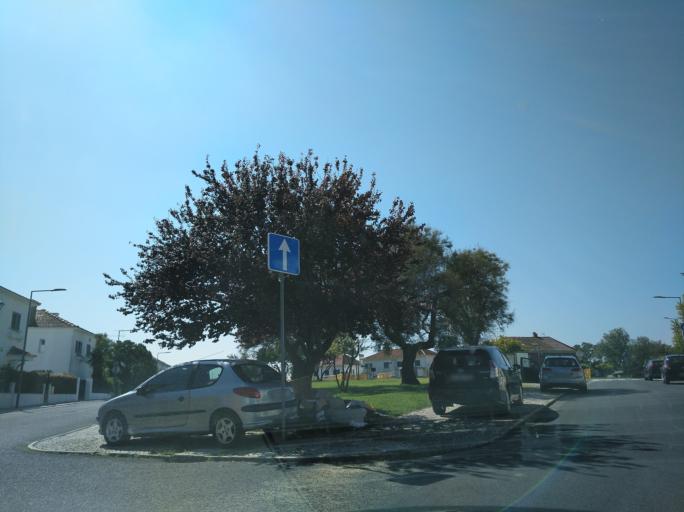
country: PT
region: Lisbon
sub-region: Lisbon
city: Lisbon
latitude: 38.7324
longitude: -9.1140
